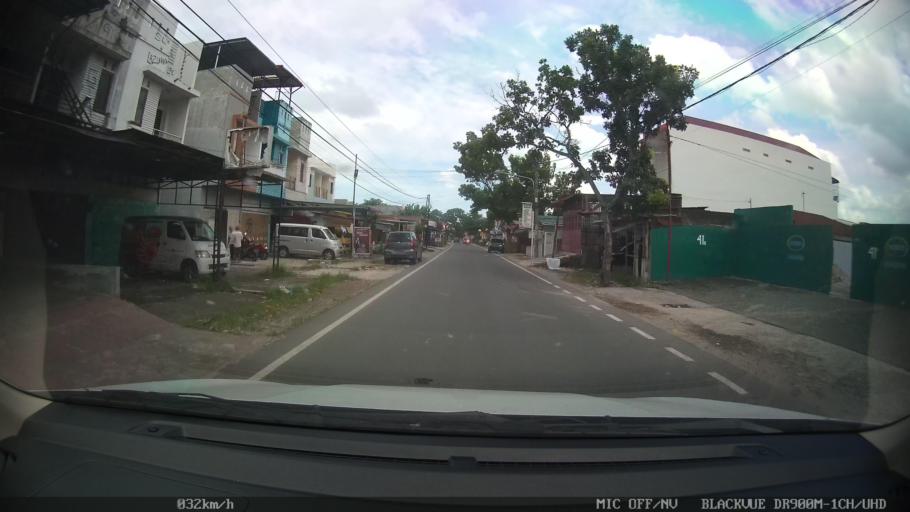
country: ID
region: North Sumatra
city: Sunggal
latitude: 3.6128
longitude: 98.6254
